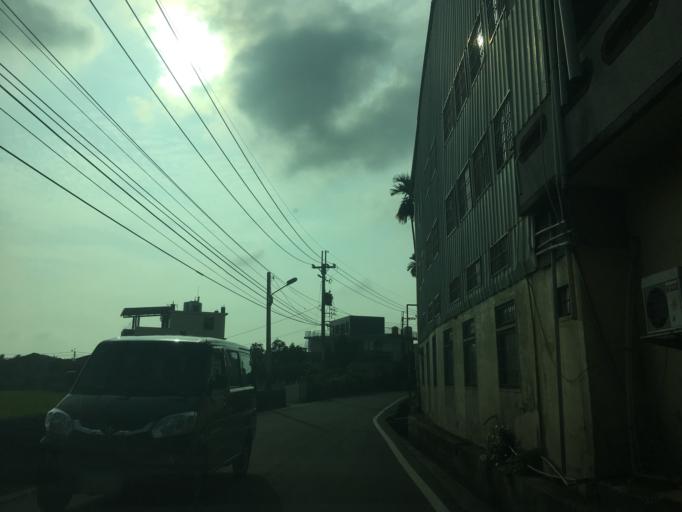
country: TW
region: Taiwan
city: Fengyuan
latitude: 24.2287
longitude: 120.7268
